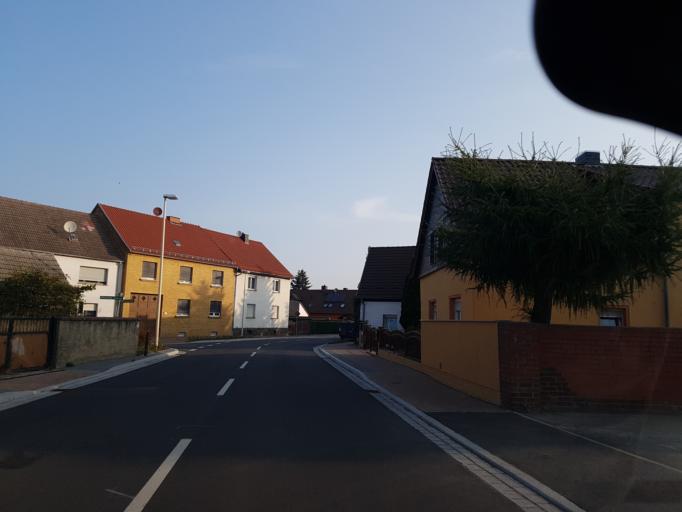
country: DE
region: Saxony-Anhalt
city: Bad Schmiedeberg
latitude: 51.7493
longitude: 12.7491
